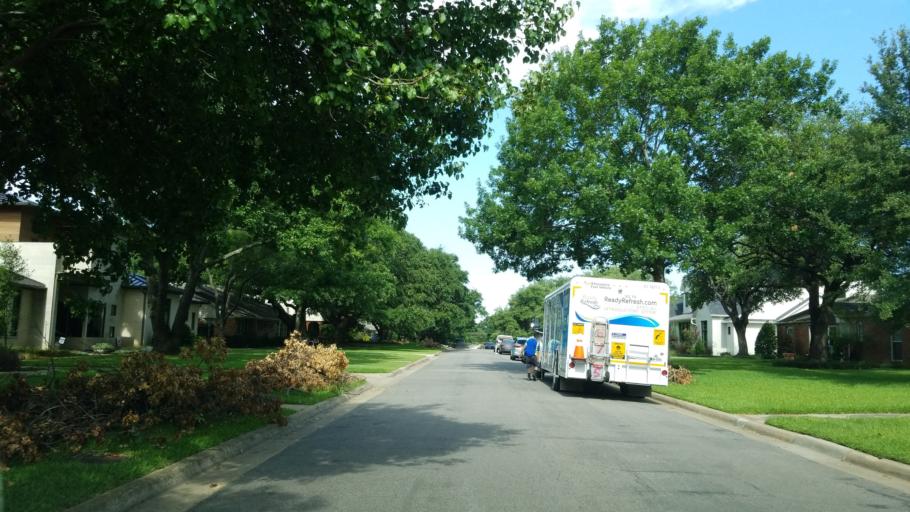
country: US
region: Texas
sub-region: Dallas County
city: Addison
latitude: 32.9043
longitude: -96.8355
